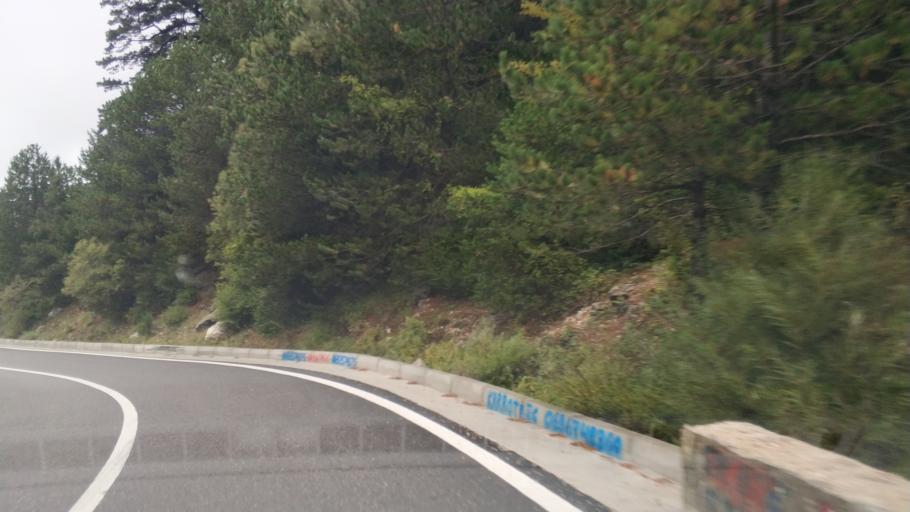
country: AL
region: Vlore
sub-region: Rrethi i Vlores
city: Brataj
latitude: 40.2042
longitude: 19.5873
